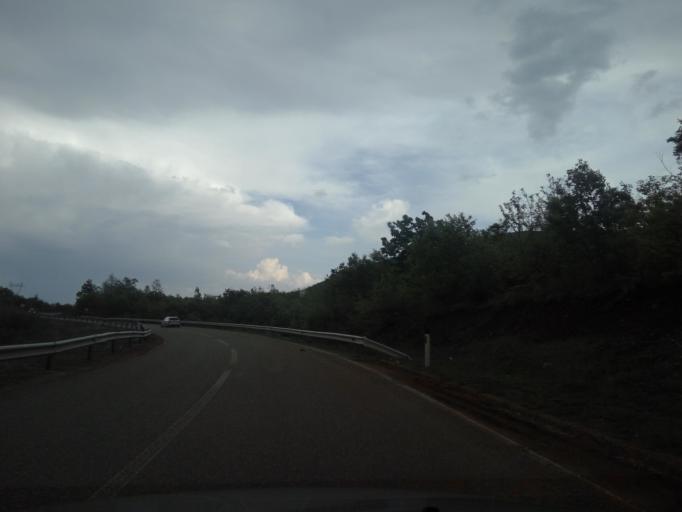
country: XK
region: Gjakova
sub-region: Komuna e Junikut
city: Junik
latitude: 42.4038
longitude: 20.2343
